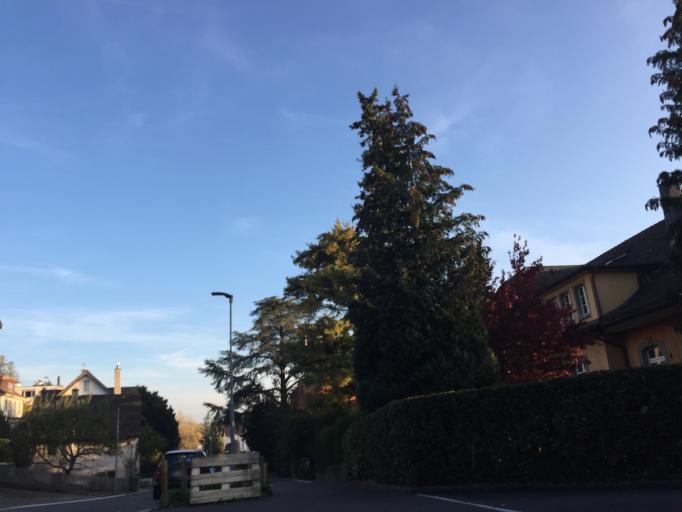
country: CH
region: Zurich
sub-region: Bezirk Zuerich
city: Zuerich (Kreis 6) / Oberstrass
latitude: 47.3845
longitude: 8.5556
